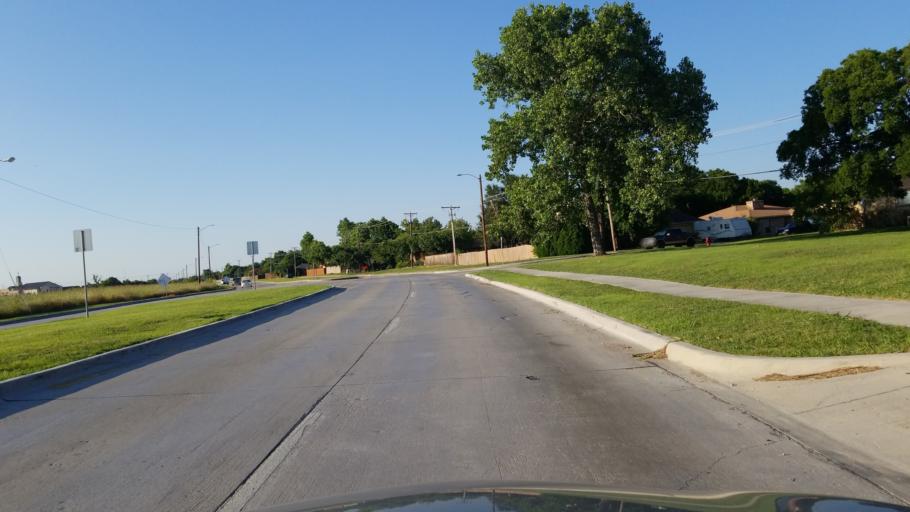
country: US
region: Texas
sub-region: Dallas County
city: Grand Prairie
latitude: 32.6854
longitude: -97.0188
